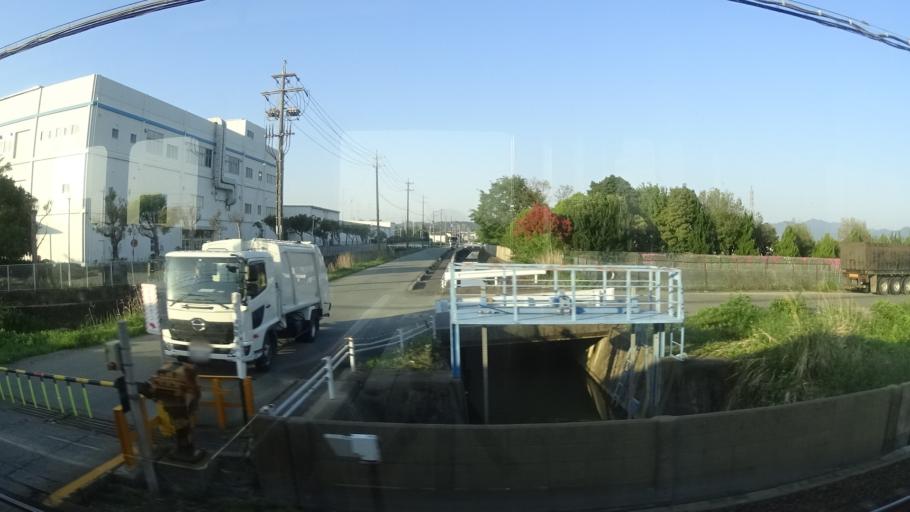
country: JP
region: Mie
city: Hisai-motomachi
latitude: 34.5593
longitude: 136.5589
